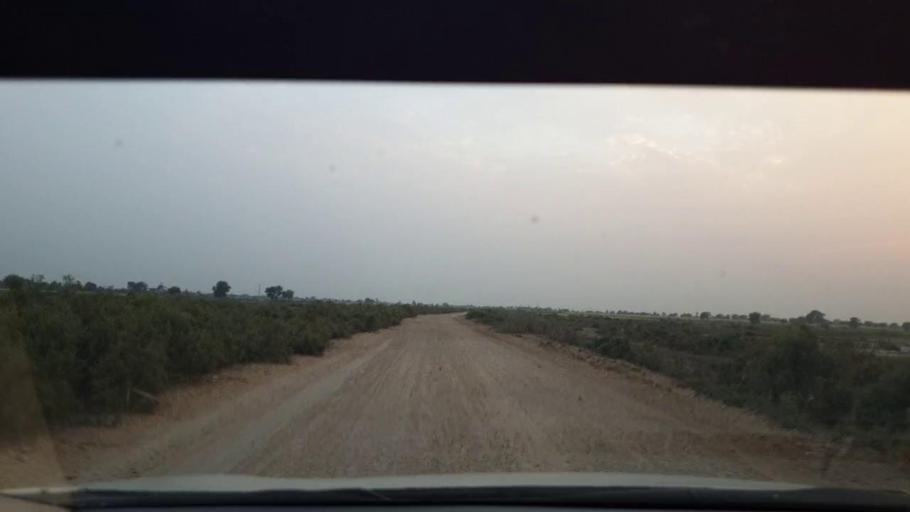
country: PK
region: Sindh
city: Berani
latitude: 25.8741
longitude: 68.7611
